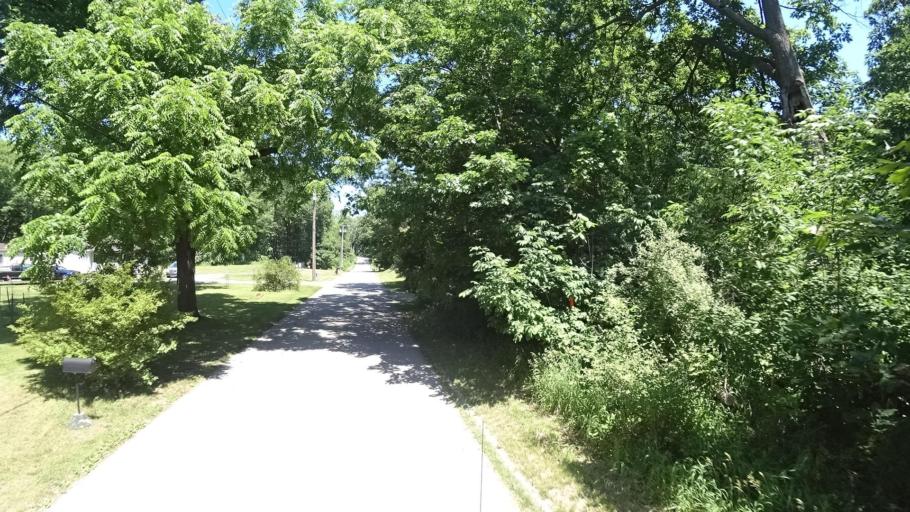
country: US
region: Indiana
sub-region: Porter County
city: Burns Harbor
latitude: 41.6048
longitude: -87.1394
